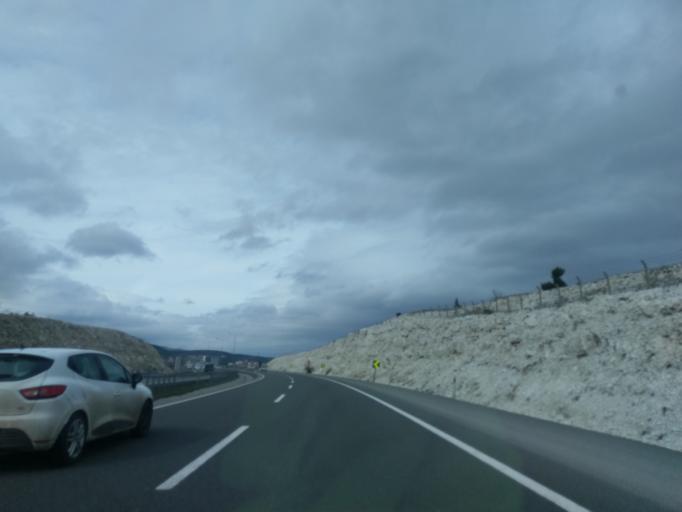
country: TR
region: Kuetahya
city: Kutahya
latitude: 39.3746
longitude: 30.0640
